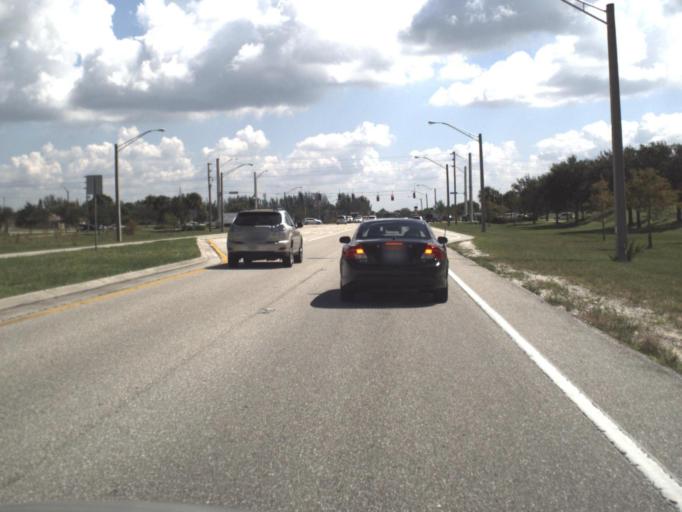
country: US
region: Florida
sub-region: Lee County
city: Cape Coral
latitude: 26.6070
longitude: -81.9931
